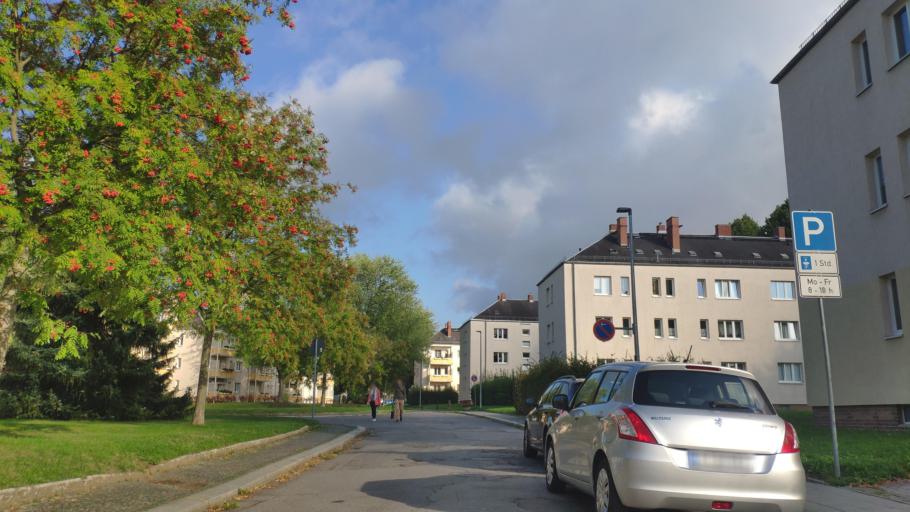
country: DE
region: Saxony
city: Chemnitz
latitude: 50.8168
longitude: 12.9524
